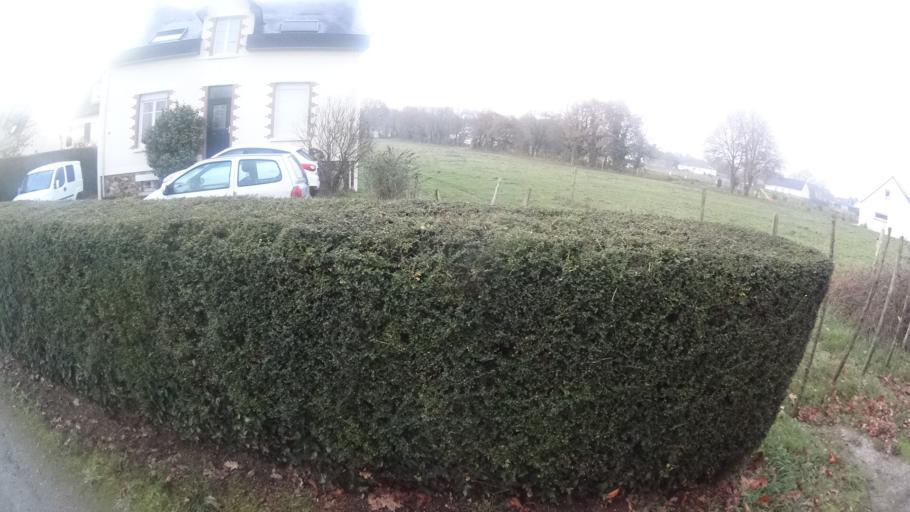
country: FR
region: Pays de la Loire
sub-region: Departement de la Loire-Atlantique
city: Saint-Nicolas-de-Redon
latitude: 47.6489
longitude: -2.0572
